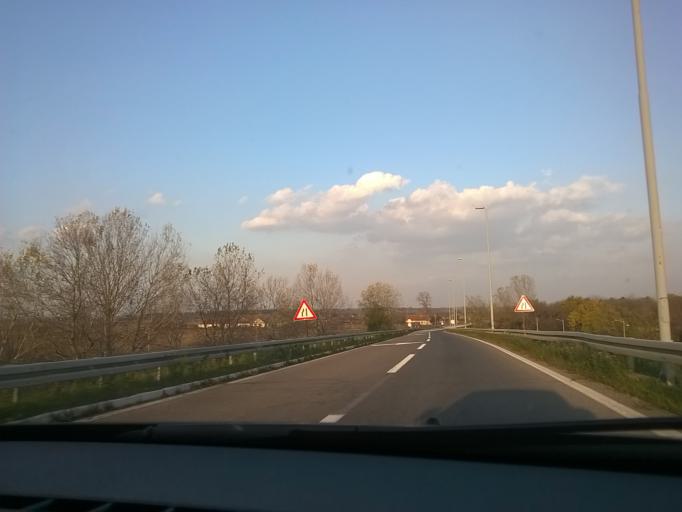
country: RS
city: Ovca
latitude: 44.8636
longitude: 20.5820
